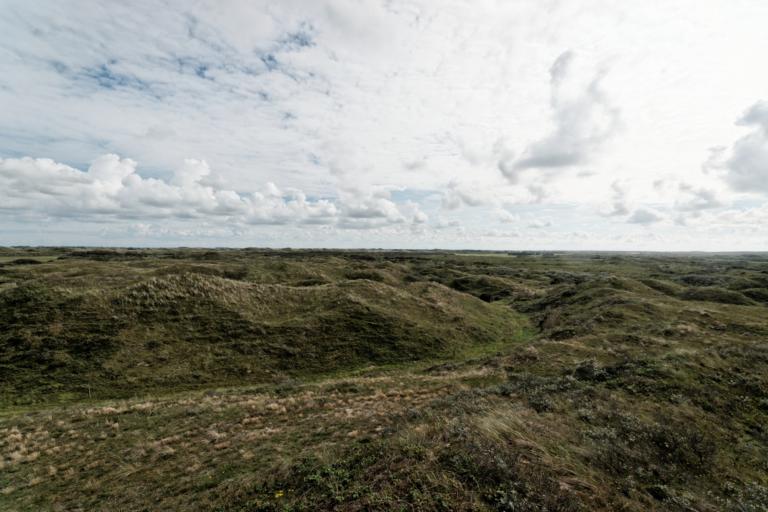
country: NL
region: North Holland
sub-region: Gemeente Texel
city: Den Burg
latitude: 53.1250
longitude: 4.7926
